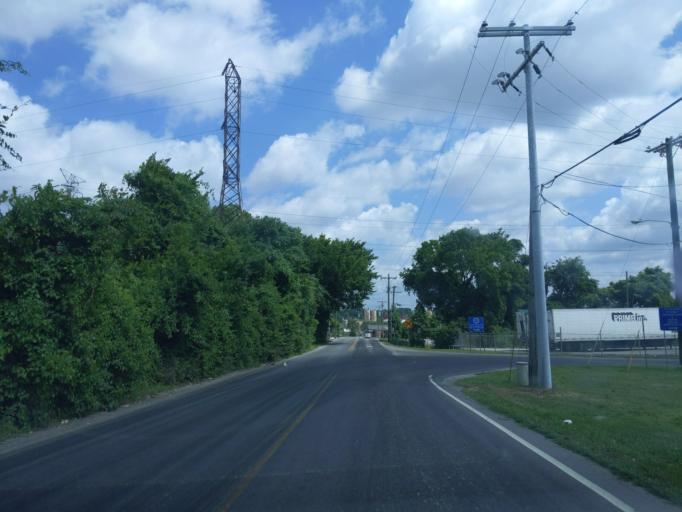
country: US
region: Tennessee
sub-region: Davidson County
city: Nashville
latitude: 36.1557
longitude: -86.7397
